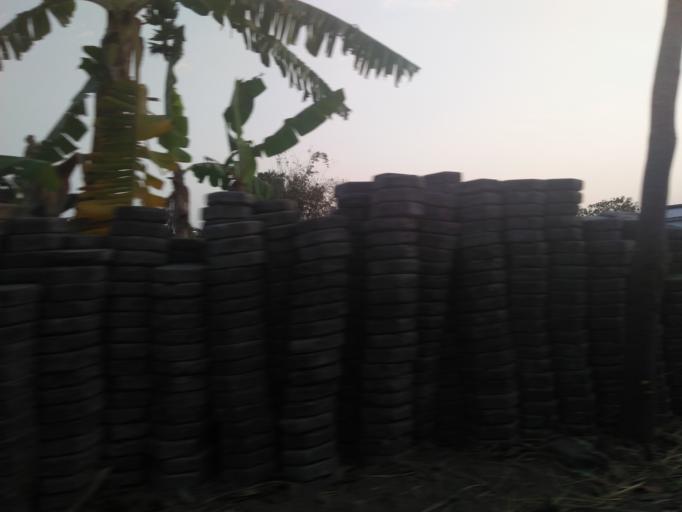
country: ID
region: Daerah Istimewa Yogyakarta
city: Sewon
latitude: -7.8467
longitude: 110.4065
